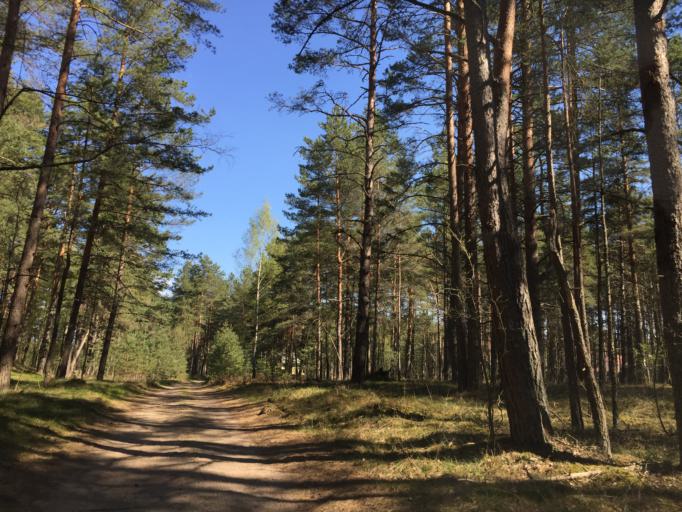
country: LV
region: Adazi
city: Adazi
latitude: 57.1106
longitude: 24.3396
